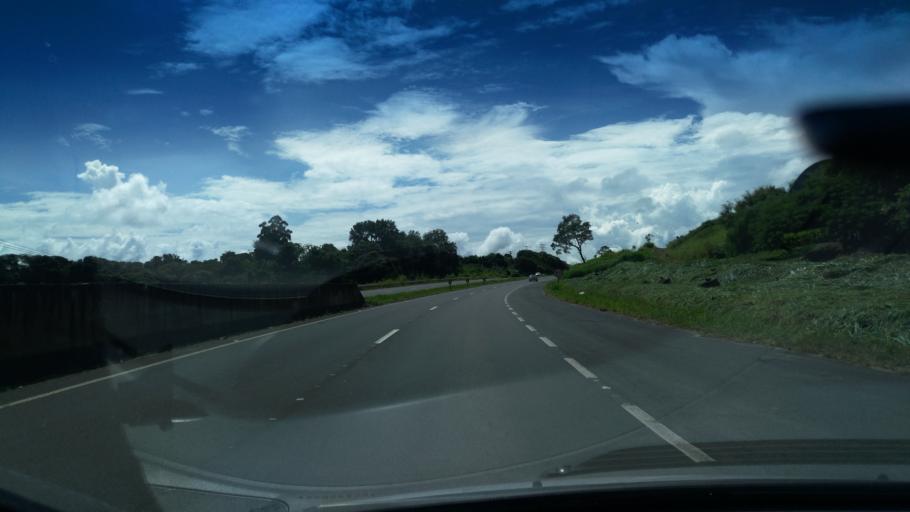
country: BR
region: Sao Paulo
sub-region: Santo Antonio Do Jardim
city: Espirito Santo do Pinhal
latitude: -22.1848
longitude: -46.7638
